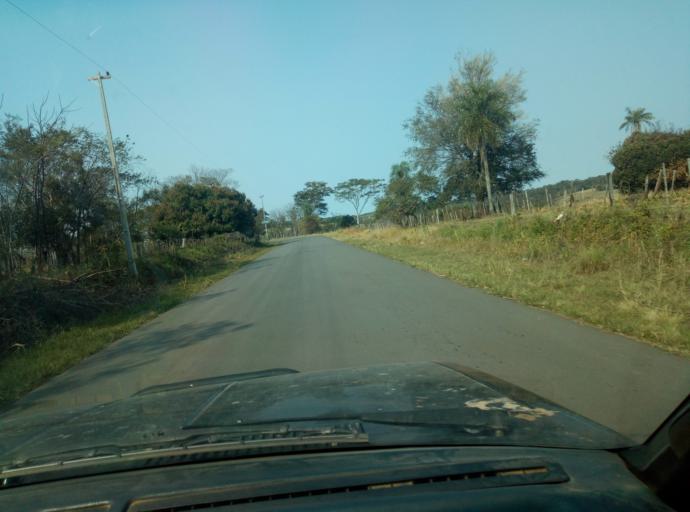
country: PY
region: Caaguazu
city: Carayao
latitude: -25.1922
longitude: -56.3108
